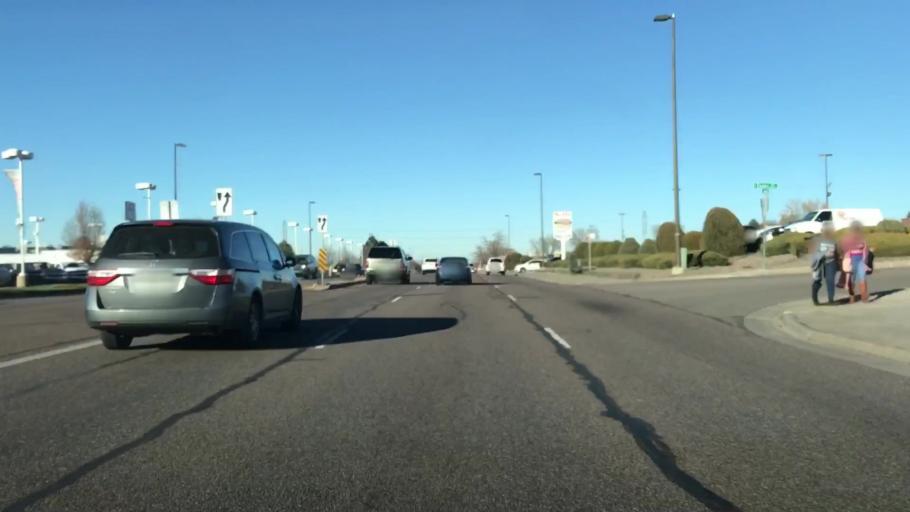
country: US
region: Colorado
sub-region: Adams County
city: Aurora
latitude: 39.6783
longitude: -104.8658
